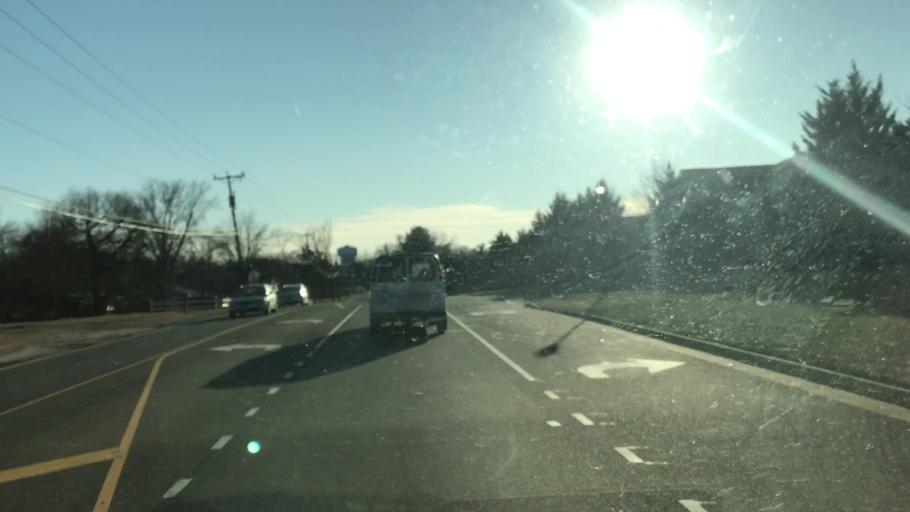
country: US
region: Virginia
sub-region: City of Fredericksburg
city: Fredericksburg
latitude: 38.2848
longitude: -77.4796
